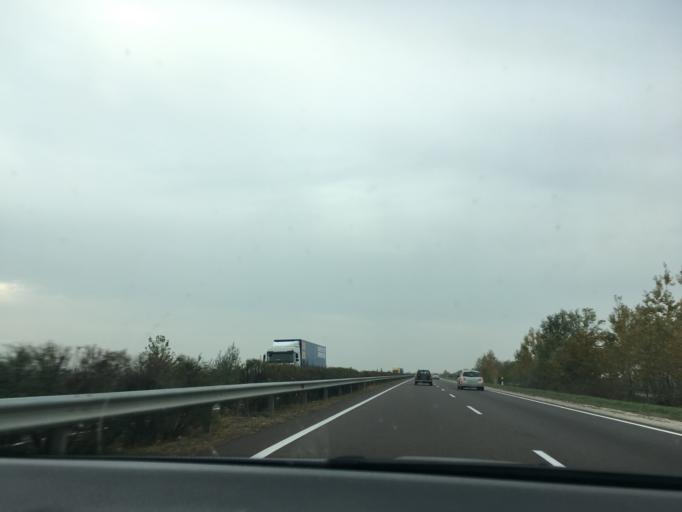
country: HU
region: Pest
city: Tortel
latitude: 47.1906
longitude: 19.8843
